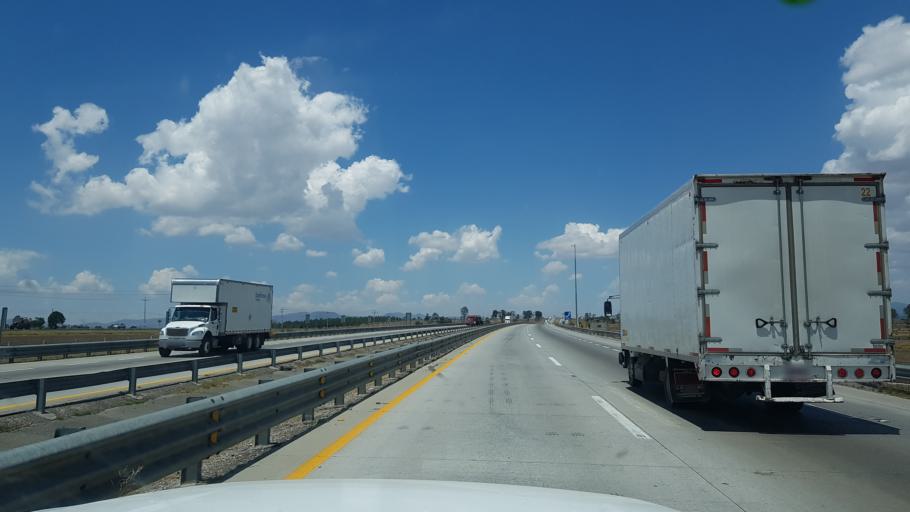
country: MX
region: Tlaxcala
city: Sanctorum
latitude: 19.5311
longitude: -98.4818
